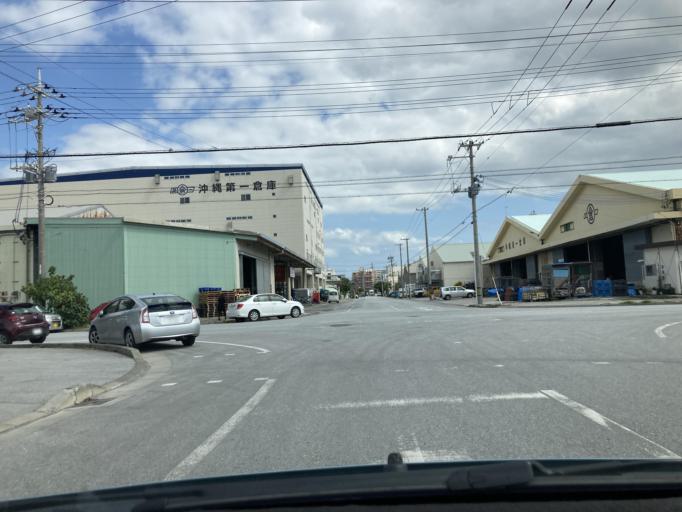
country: JP
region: Okinawa
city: Naha-shi
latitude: 26.2427
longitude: 127.6730
